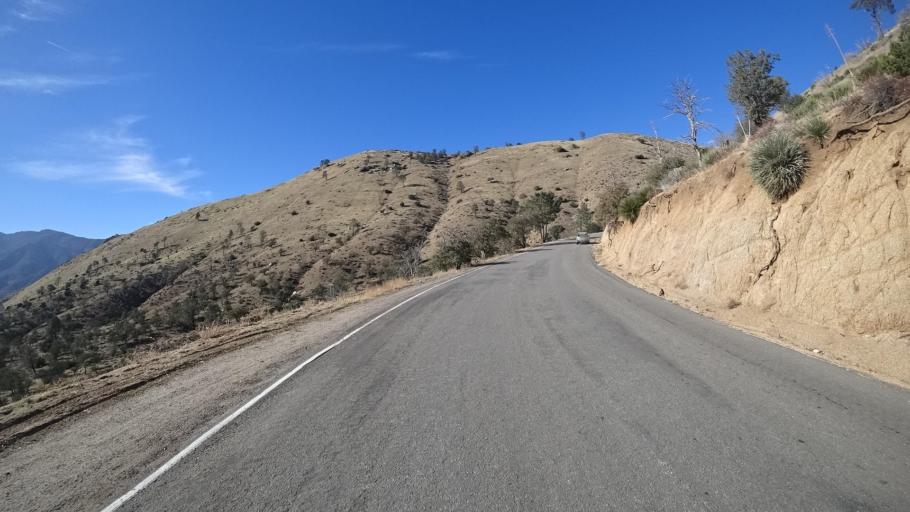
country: US
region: California
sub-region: Kern County
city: Bodfish
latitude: 35.5664
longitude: -118.5054
